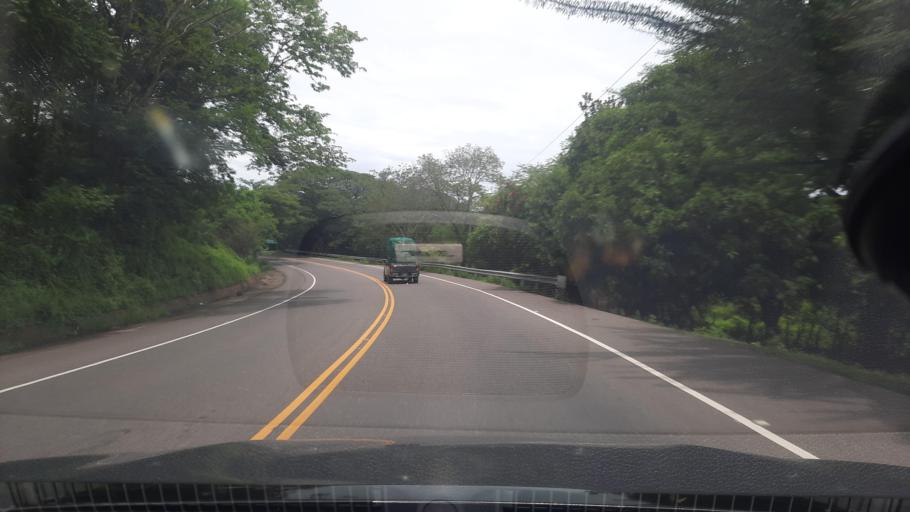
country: HN
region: Valle
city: Goascoran
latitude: 13.5586
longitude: -87.6589
